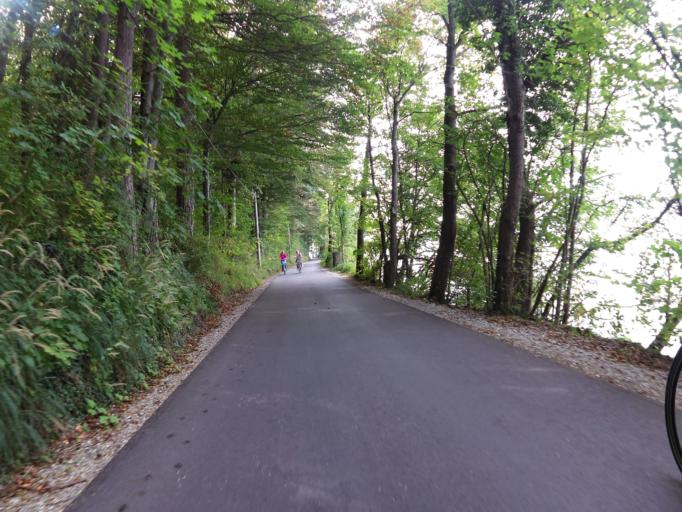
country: DE
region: Bavaria
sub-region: Upper Bavaria
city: Berg
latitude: 47.9439
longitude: 11.3394
